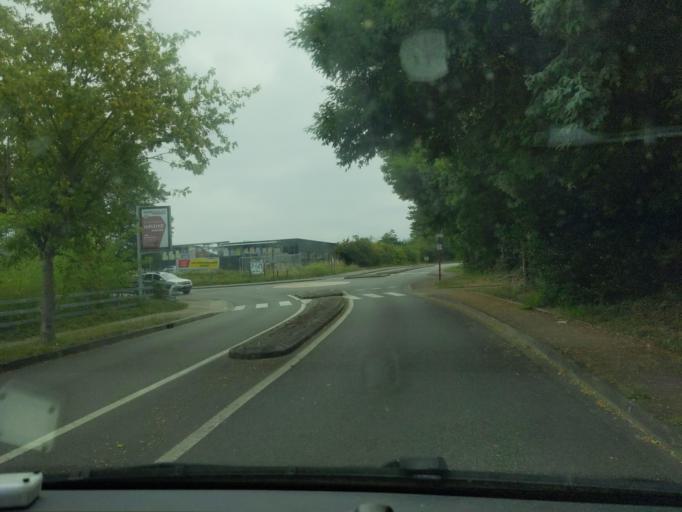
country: FR
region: Midi-Pyrenees
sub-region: Departement de la Haute-Garonne
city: Auzeville-Tolosane
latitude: 43.5355
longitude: 1.4769
